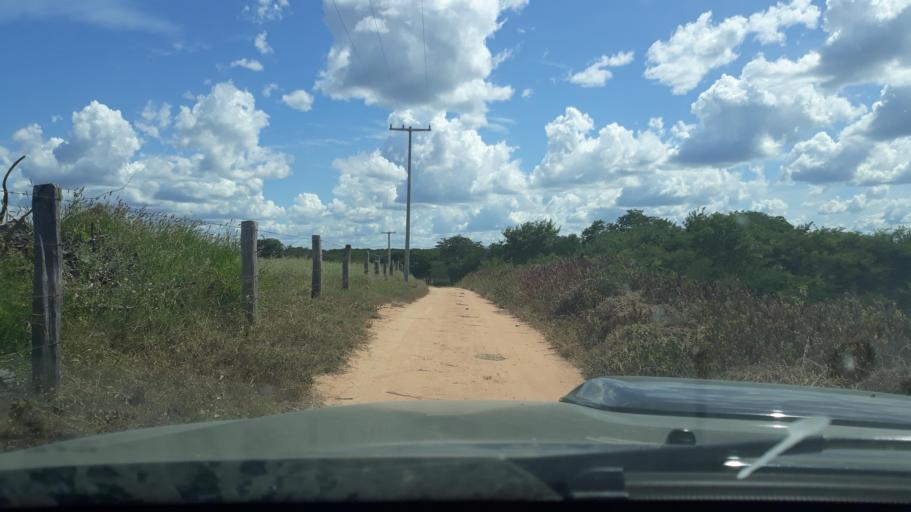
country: BR
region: Bahia
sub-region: Riacho De Santana
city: Riacho de Santana
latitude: -13.8663
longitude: -43.0766
